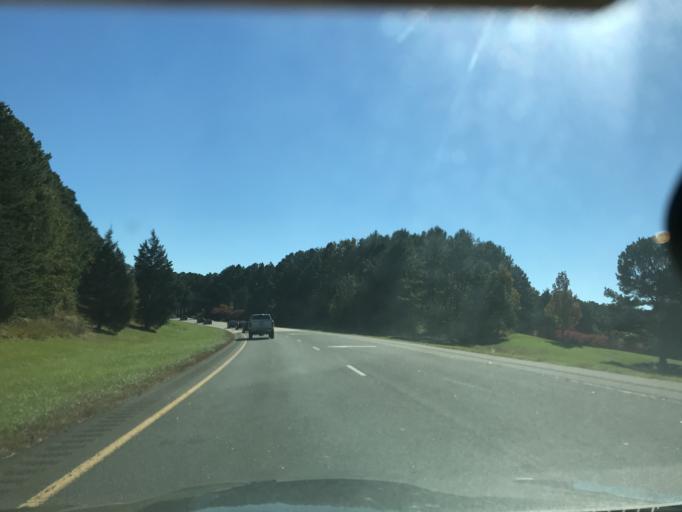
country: US
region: North Carolina
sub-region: Wake County
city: Morrisville
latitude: 35.9022
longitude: -78.8721
